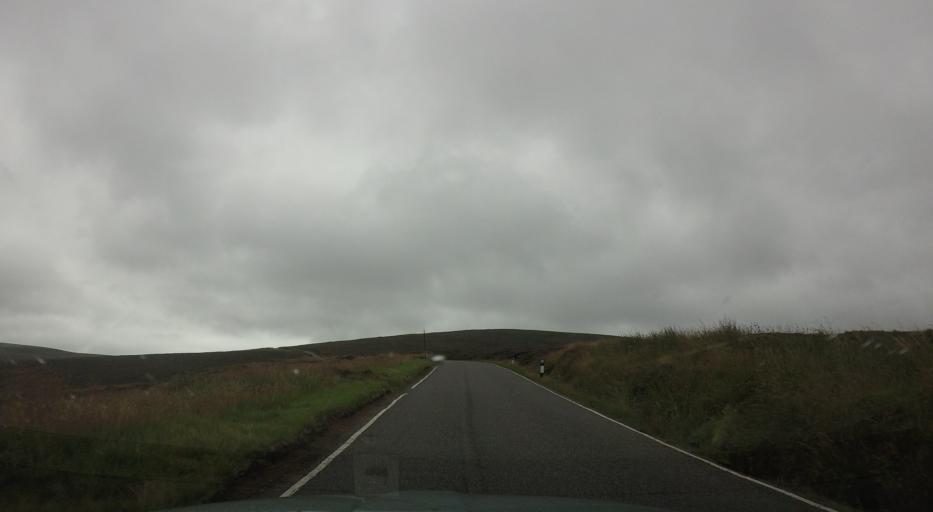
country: GB
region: Scotland
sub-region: Aberdeenshire
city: Banchory
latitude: 56.9399
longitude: -2.5747
